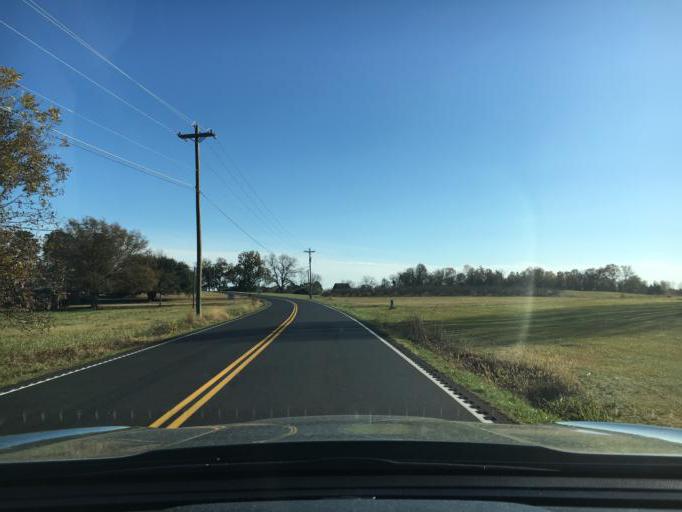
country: US
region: South Carolina
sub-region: Spartanburg County
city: Inman Mills
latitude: 35.0347
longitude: -82.1288
